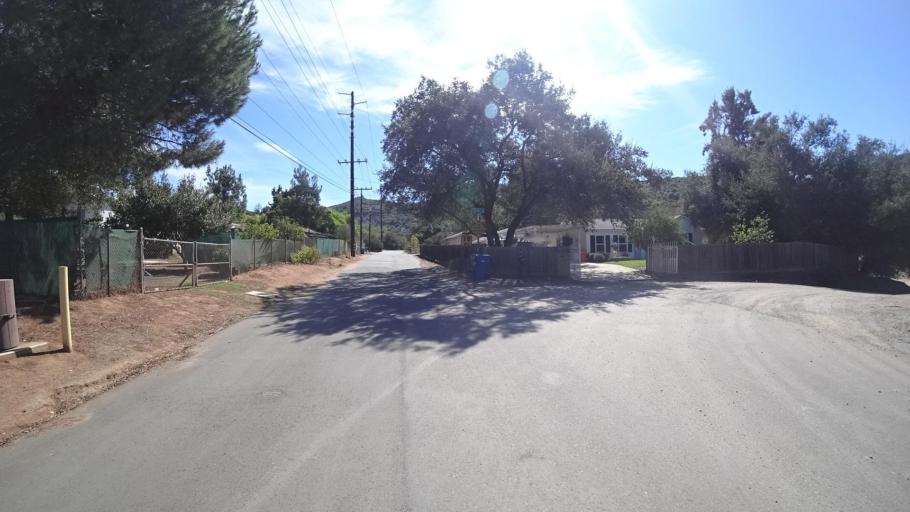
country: US
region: California
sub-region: San Diego County
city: Crest
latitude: 32.8375
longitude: -116.8736
